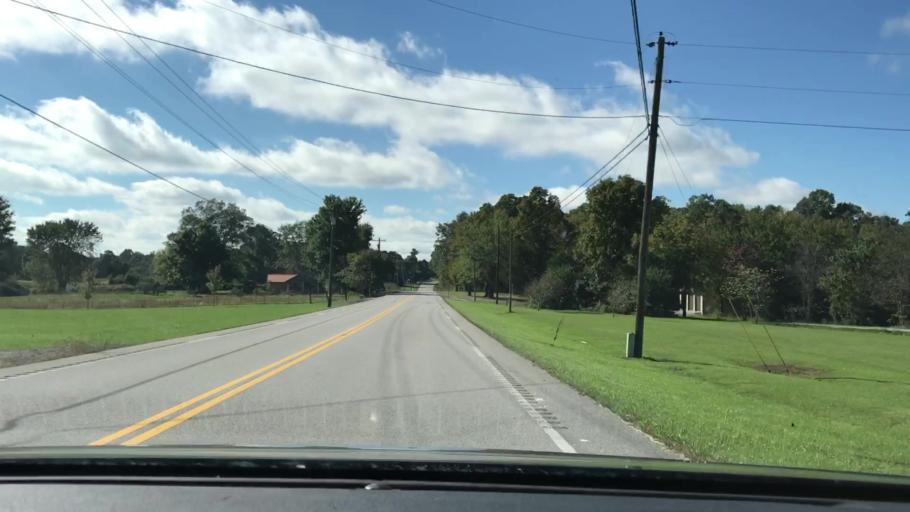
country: US
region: Tennessee
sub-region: Fentress County
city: Jamestown
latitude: 36.3730
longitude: -84.8630
